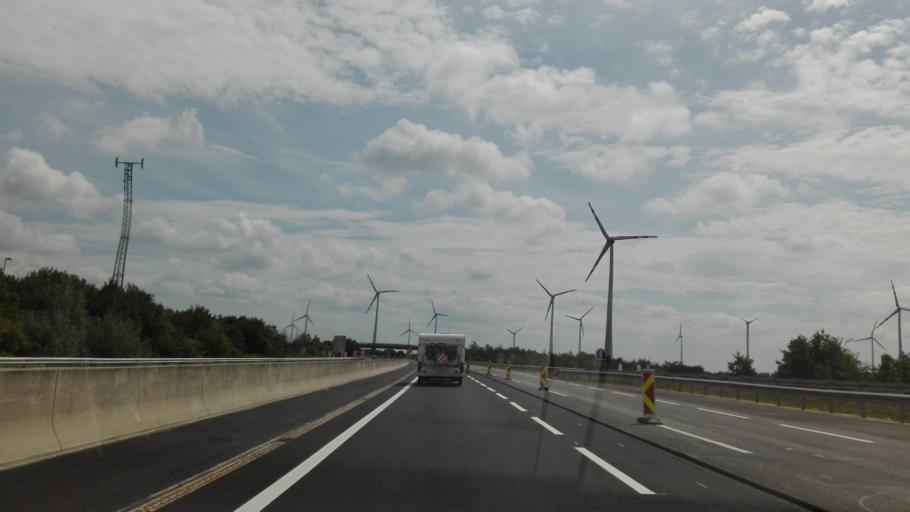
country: AT
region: Burgenland
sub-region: Politischer Bezirk Neusiedl am See
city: Nickelsdorf
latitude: 47.9204
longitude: 17.0413
